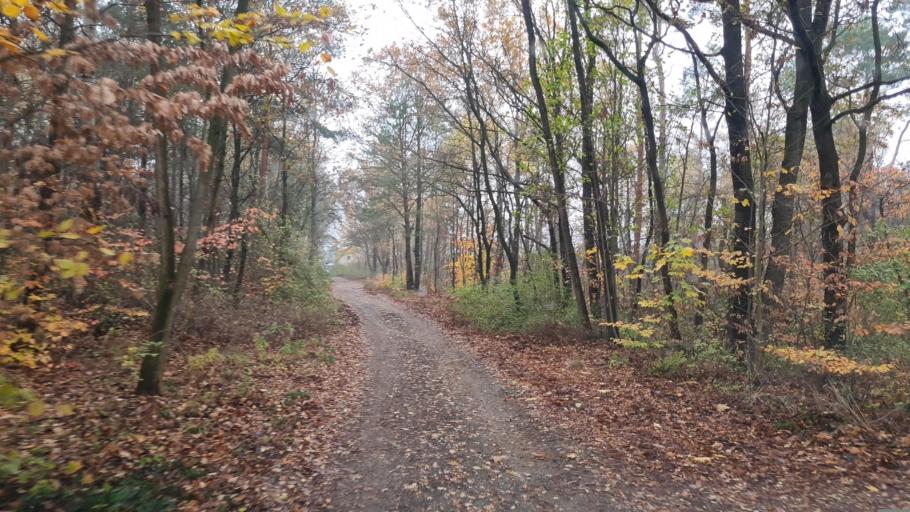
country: DE
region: Brandenburg
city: Lauchhammer
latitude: 51.5008
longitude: 13.7863
